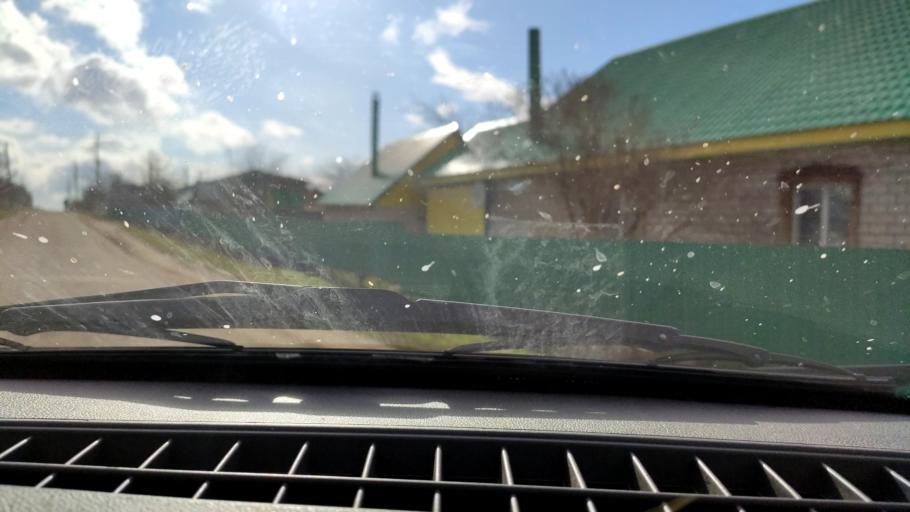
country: RU
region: Bashkortostan
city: Chekmagush
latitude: 55.1463
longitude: 54.6429
